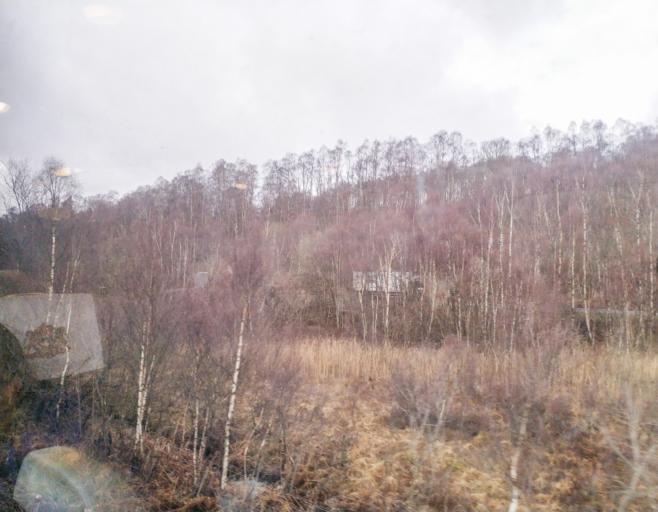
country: GB
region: Scotland
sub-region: Highland
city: Spean Bridge
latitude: 56.8863
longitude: -4.8214
